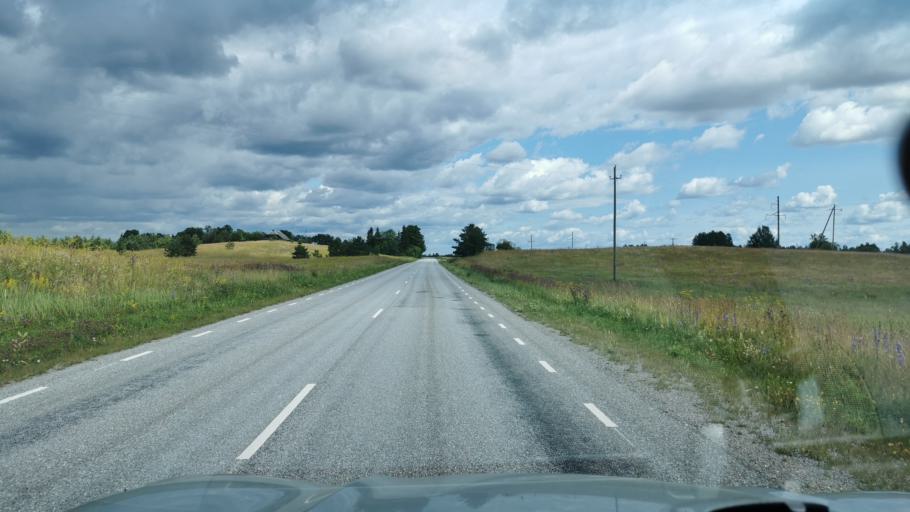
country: EE
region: Harju
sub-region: Kuusalu vald
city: Kuusalu
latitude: 59.2145
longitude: 25.6033
